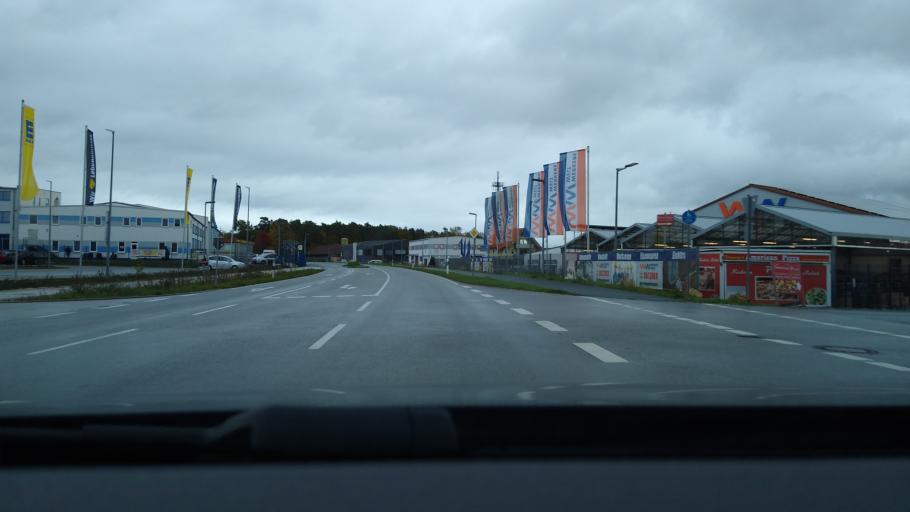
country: DE
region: Bavaria
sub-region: Regierungsbezirk Mittelfranken
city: Hemhofen
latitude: 49.6923
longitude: 10.9426
